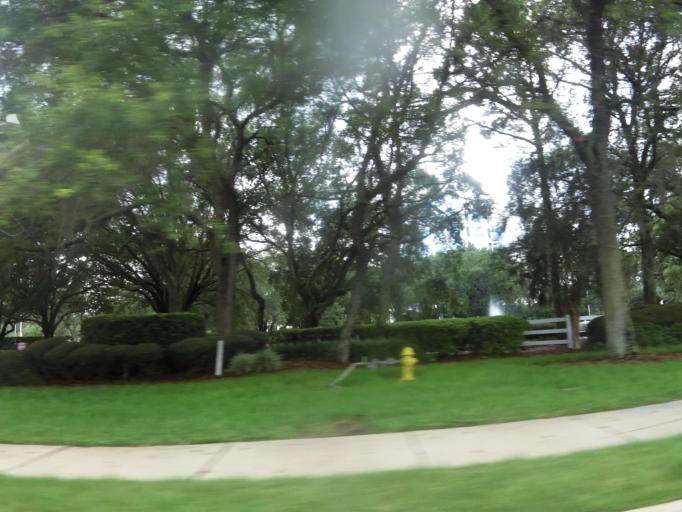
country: US
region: Florida
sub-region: Saint Johns County
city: Ponte Vedra Beach
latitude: 30.2546
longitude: -81.4372
